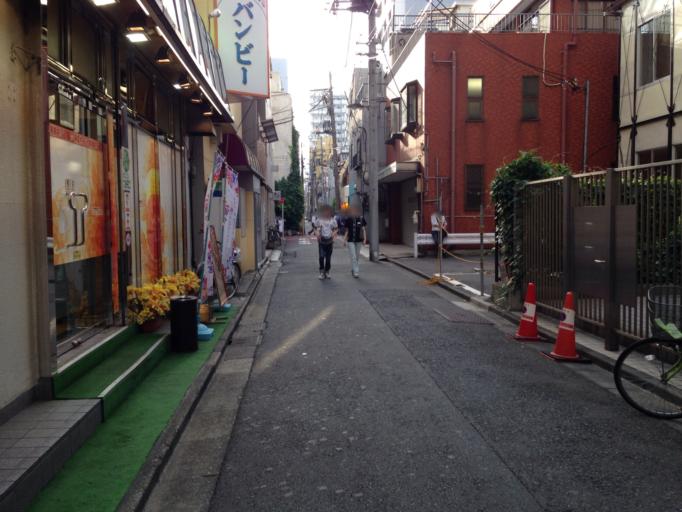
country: JP
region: Tokyo
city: Urayasu
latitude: 35.6720
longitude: 139.7970
